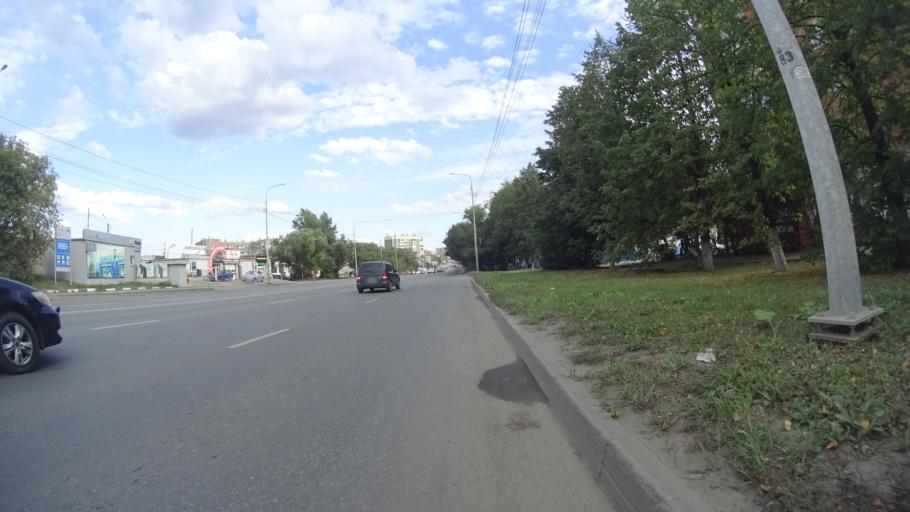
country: RU
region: Chelyabinsk
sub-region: Gorod Chelyabinsk
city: Chelyabinsk
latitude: 55.2017
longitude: 61.3271
